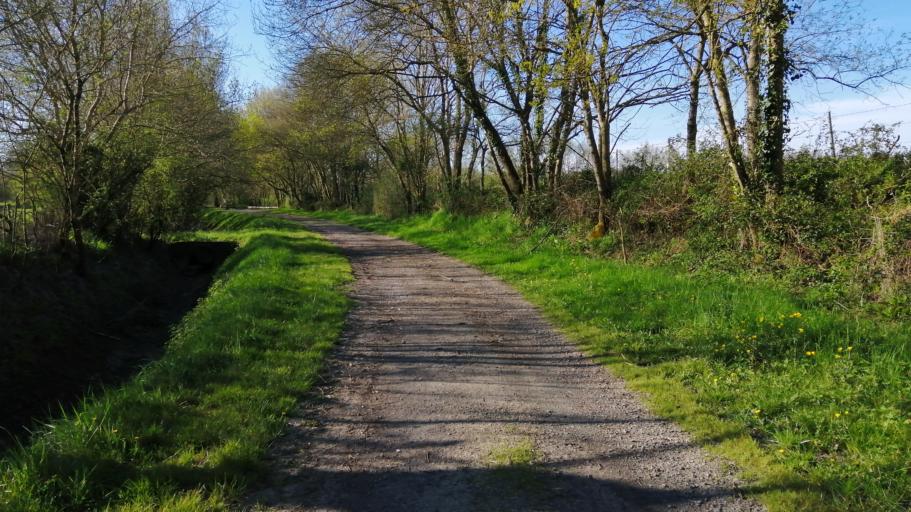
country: FR
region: Pays de la Loire
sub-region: Departement de la Loire-Atlantique
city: Saint-Gereon
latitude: 47.3588
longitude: -1.2017
